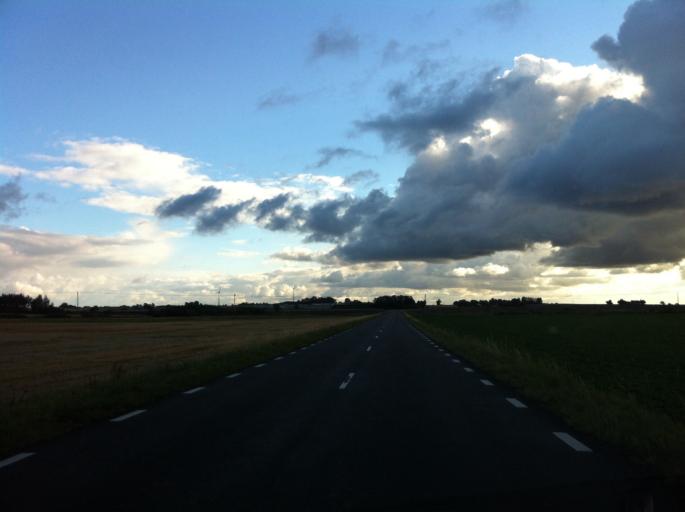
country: SE
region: Skane
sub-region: Svalovs Kommun
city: Svaloev
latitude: 55.9122
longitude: 13.2000
